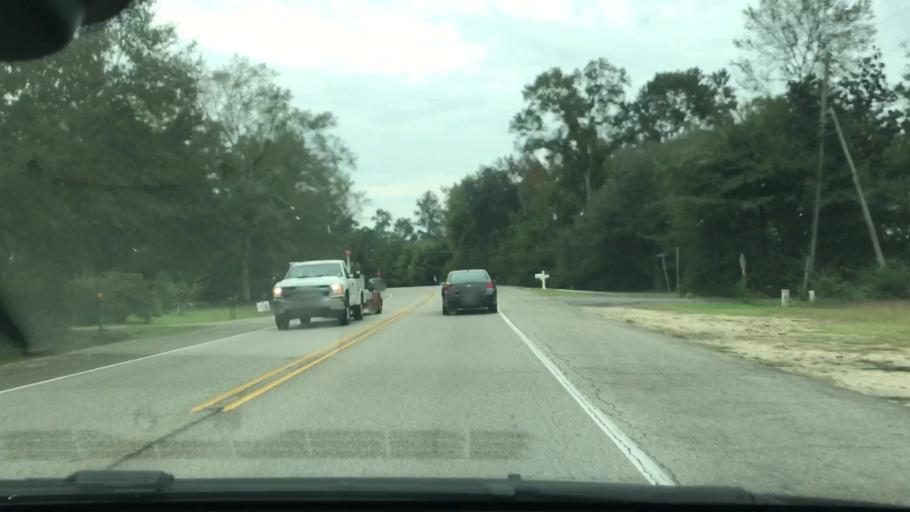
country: US
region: Louisiana
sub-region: Saint Tammany Parish
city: Pearl River
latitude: 30.3769
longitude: -89.7687
